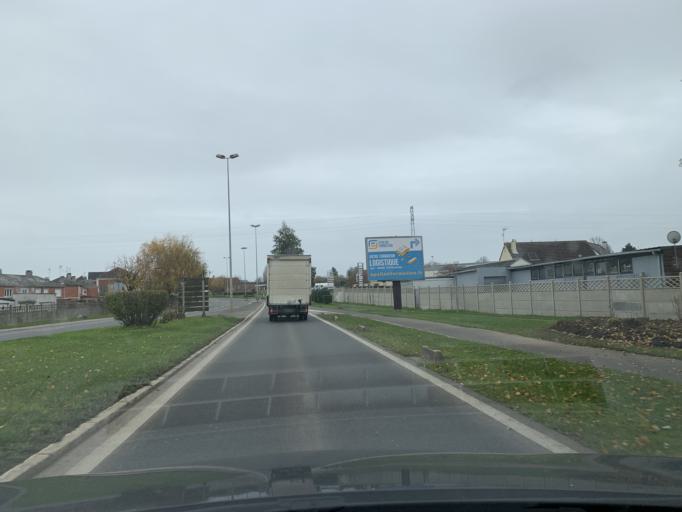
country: FR
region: Nord-Pas-de-Calais
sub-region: Departement du Nord
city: Neuville-Saint-Remy
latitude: 50.1910
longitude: 3.2145
